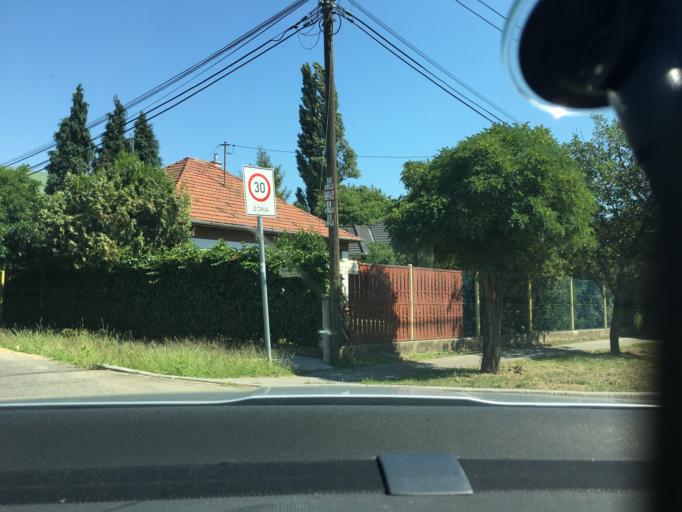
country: HU
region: Budapest
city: Budapest XVI. keruelet
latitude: 47.5047
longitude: 19.1918
